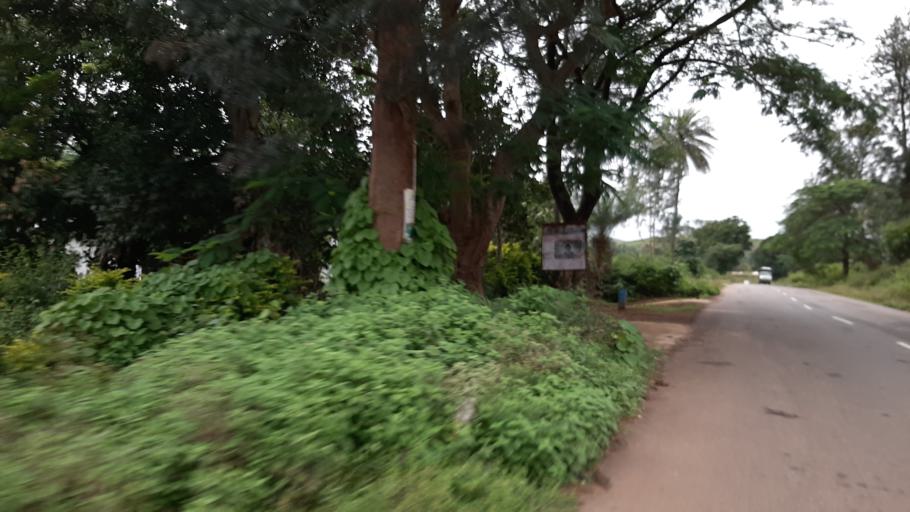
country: IN
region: Andhra Pradesh
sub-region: Vizianagaram District
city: Salur
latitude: 18.3013
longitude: 82.9108
